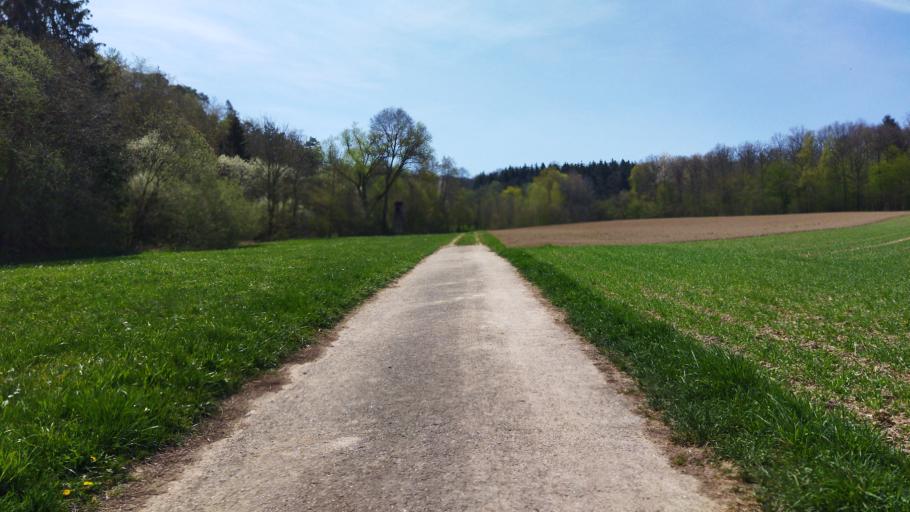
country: DE
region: Baden-Wuerttemberg
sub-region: Regierungsbezirk Stuttgart
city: Pfaffenhofen
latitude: 49.0851
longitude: 8.9657
